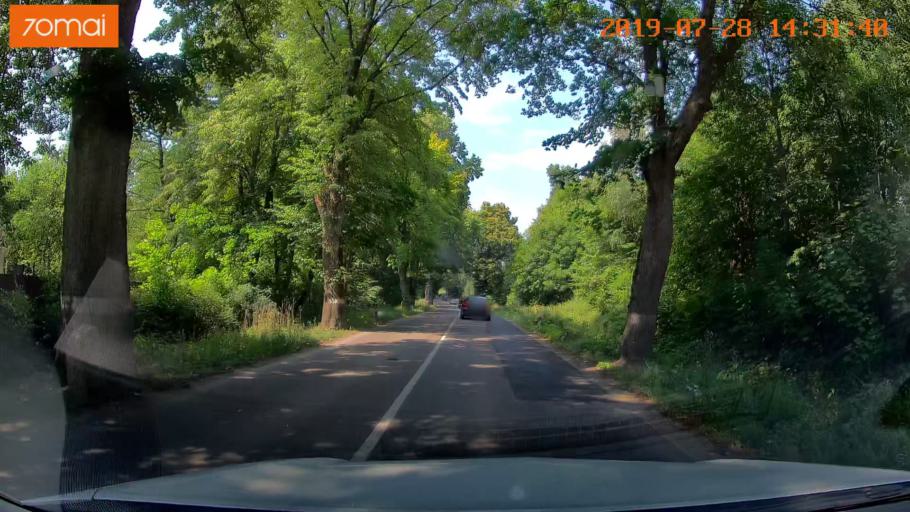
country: RU
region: Kaliningrad
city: Primorsk
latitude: 54.8079
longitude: 20.0494
